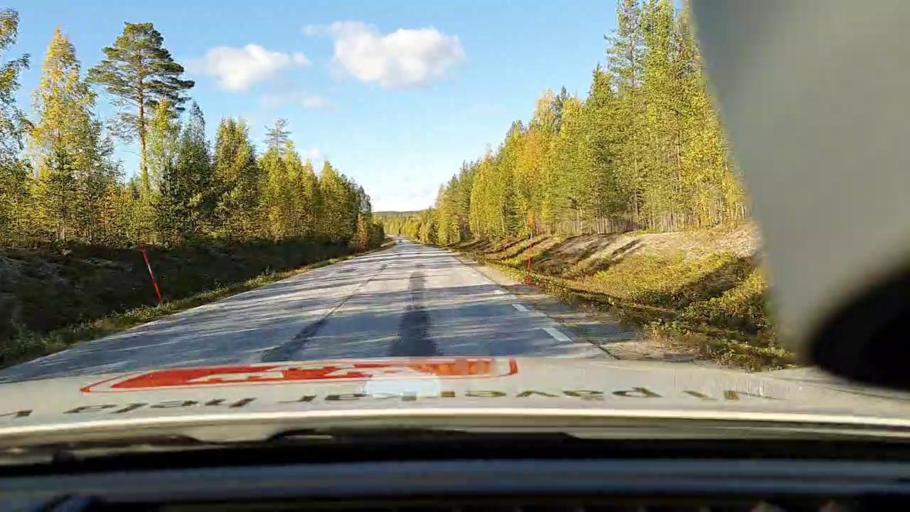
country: SE
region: Norrbotten
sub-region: Pitea Kommun
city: Norrfjarden
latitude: 65.4560
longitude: 21.4554
